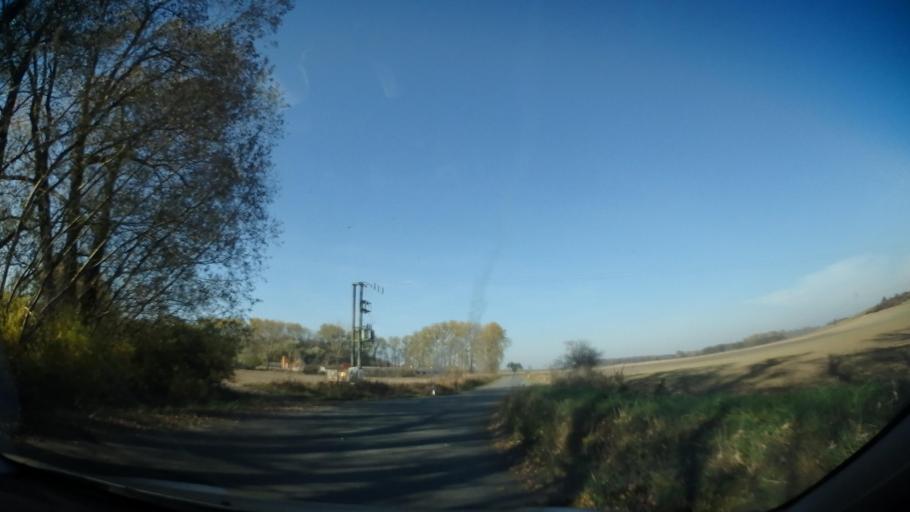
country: CZ
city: Ceske Mezirici
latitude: 50.2359
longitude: 16.0363
